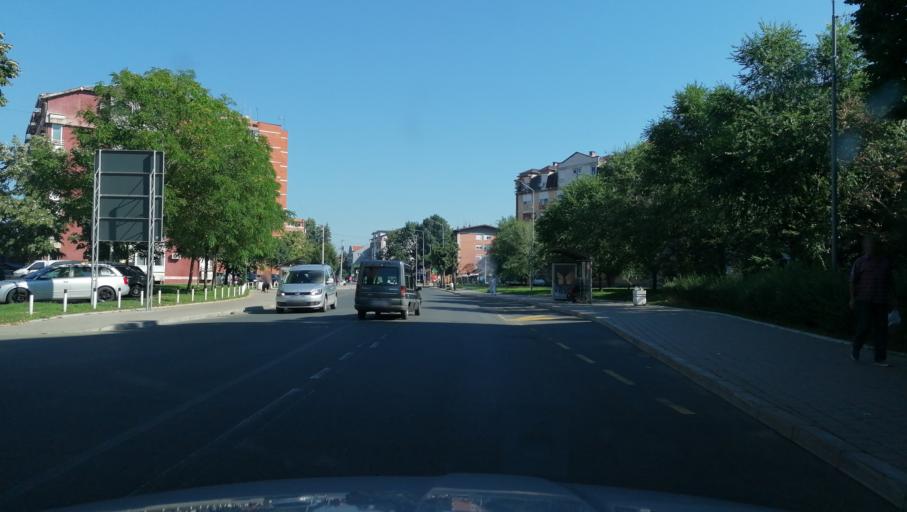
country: RS
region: Central Serbia
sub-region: Rasinski Okrug
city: Krusevac
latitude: 43.5717
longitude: 21.3382
